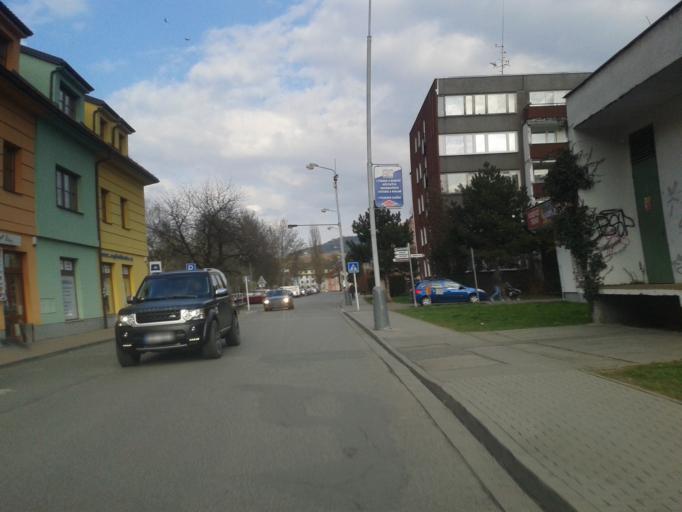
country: CZ
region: Central Bohemia
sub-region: Okres Beroun
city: Beroun
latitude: 49.9620
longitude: 14.0731
